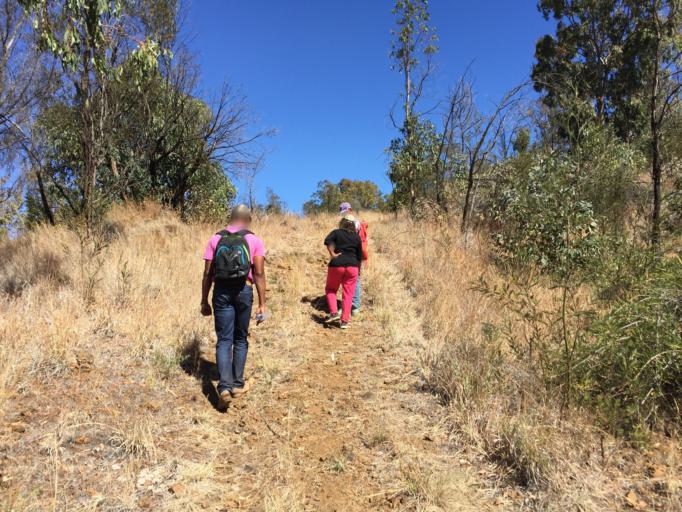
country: CV
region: Mosteiros
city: Porto dos Mosteiros
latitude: 15.0077
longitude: -24.3631
